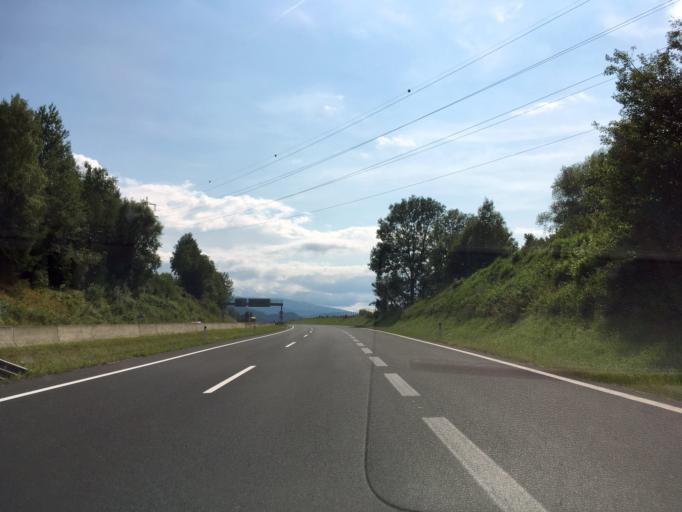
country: AT
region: Styria
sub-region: Politischer Bezirk Bruck-Muerzzuschlag
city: Muerzzuschlag
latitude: 47.5866
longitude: 15.6626
